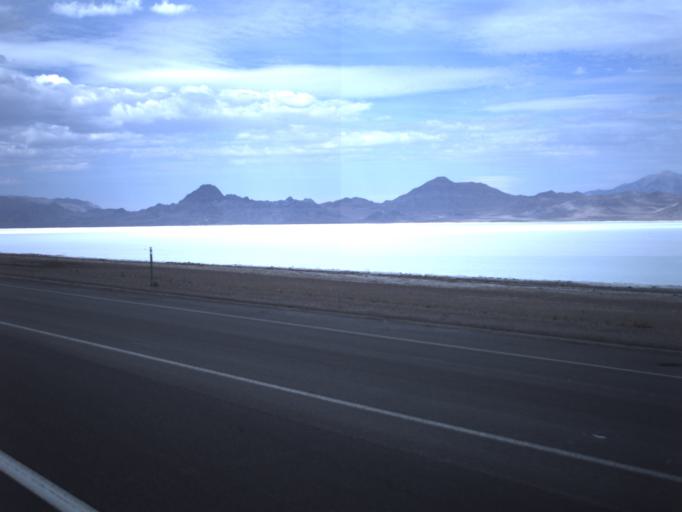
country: US
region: Utah
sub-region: Tooele County
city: Wendover
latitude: 40.7395
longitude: -113.8549
